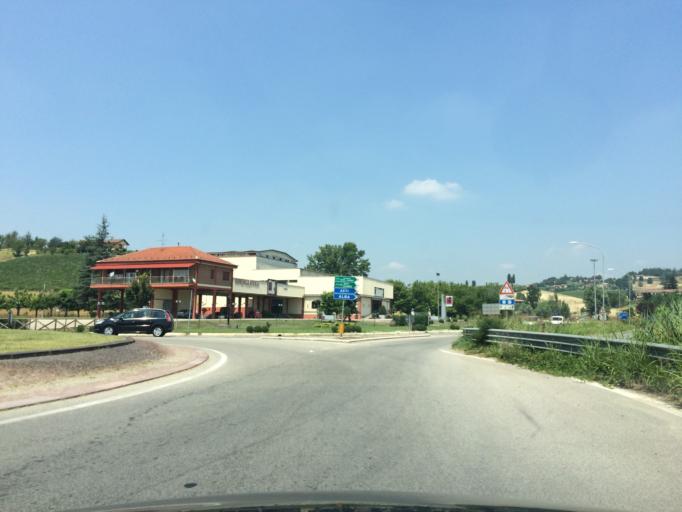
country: IT
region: Piedmont
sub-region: Provincia di Asti
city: Castelnuovo Calcea
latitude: 44.7772
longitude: 8.2787
